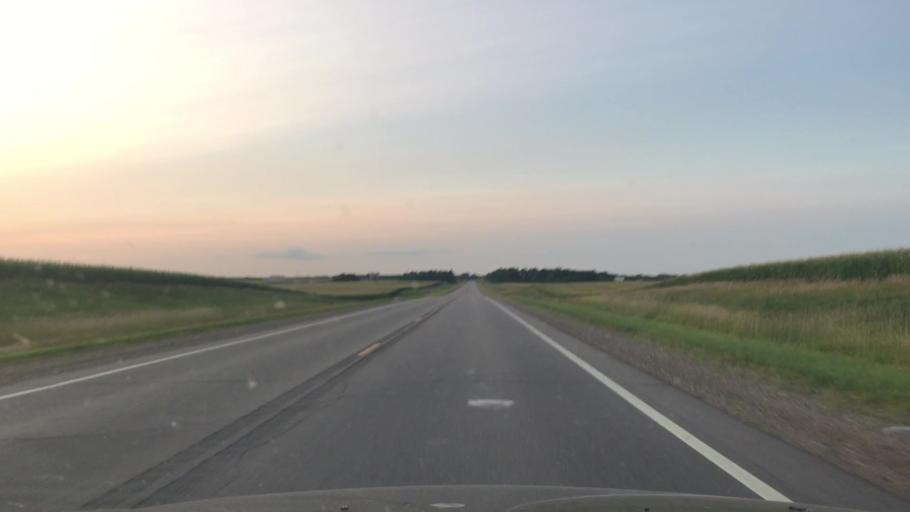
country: US
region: Minnesota
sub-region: Redwood County
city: Redwood Falls
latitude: 44.5077
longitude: -95.1179
